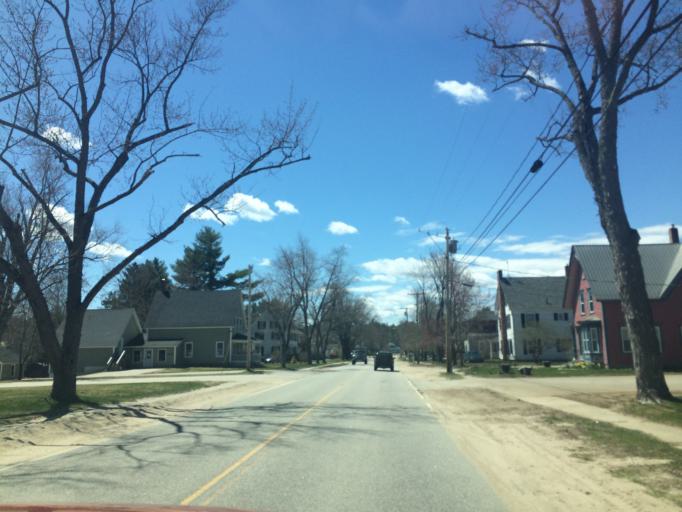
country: US
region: Maine
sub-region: Oxford County
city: Porter
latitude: 43.8105
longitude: -70.8855
